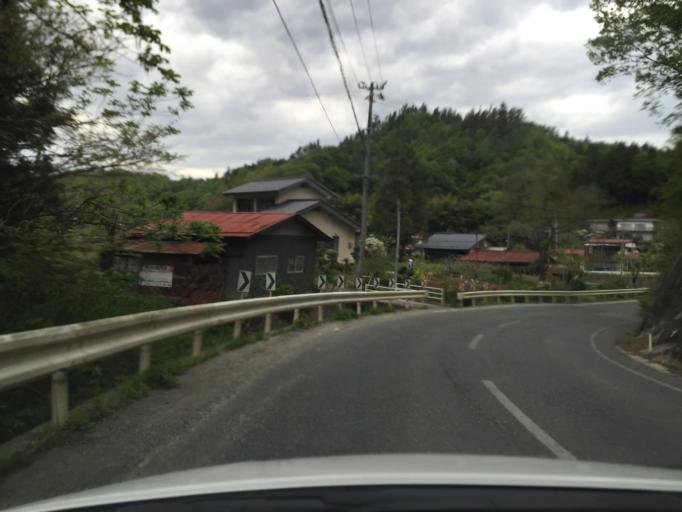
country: JP
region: Fukushima
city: Yanagawamachi-saiwaicho
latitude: 37.7583
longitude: 140.6444
